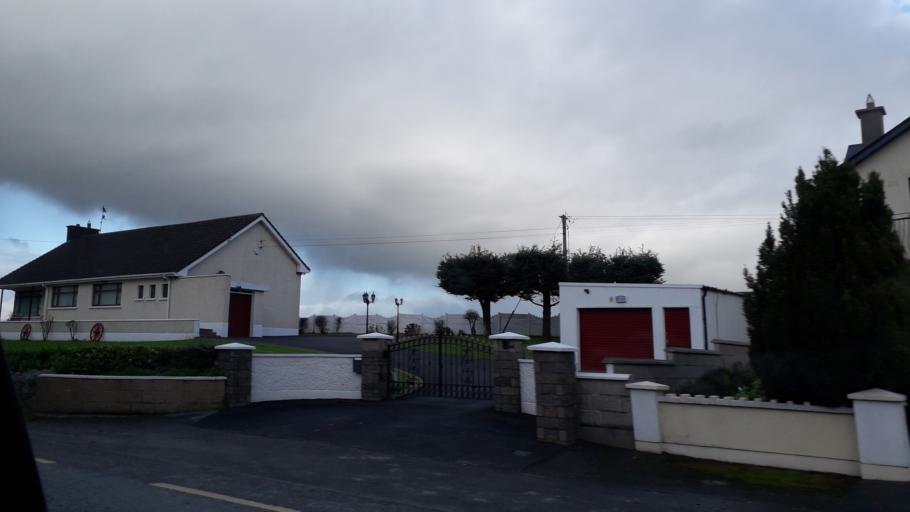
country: IE
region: Leinster
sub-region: Lu
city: Ardee
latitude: 53.8389
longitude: -6.5391
